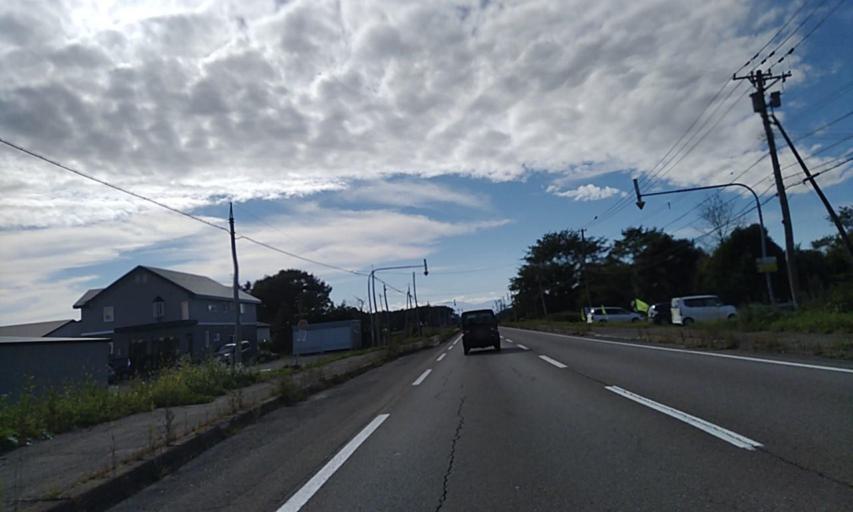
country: JP
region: Hokkaido
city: Obihiro
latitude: 42.9181
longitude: 143.2933
